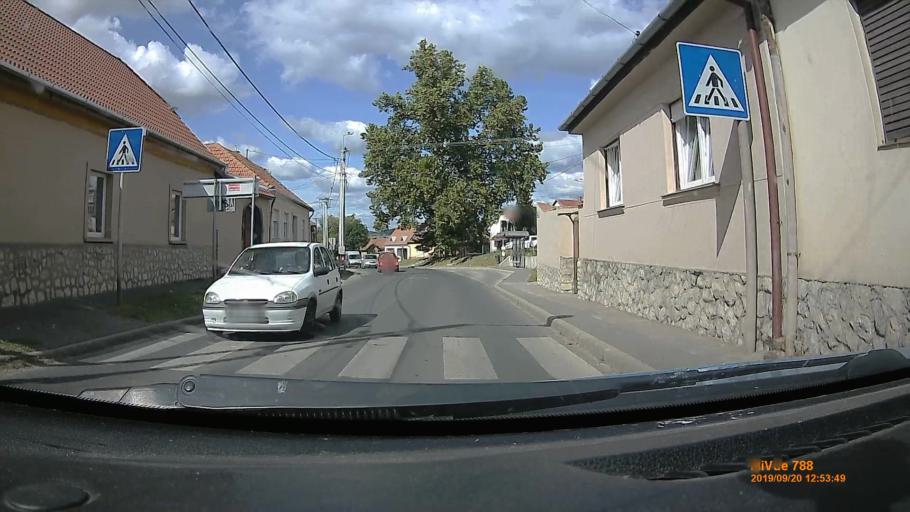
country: HU
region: Heves
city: Eger
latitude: 47.9086
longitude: 20.3790
